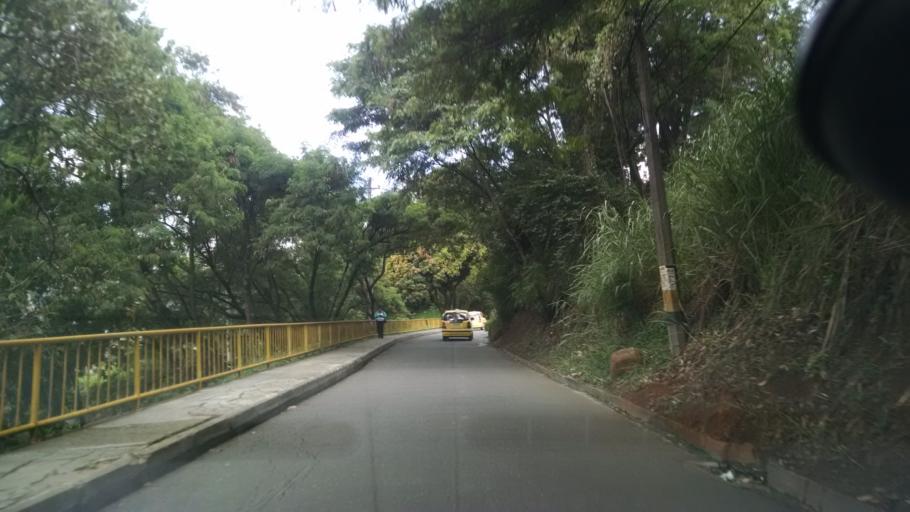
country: CO
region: Antioquia
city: Medellin
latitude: 6.2149
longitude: -75.5740
